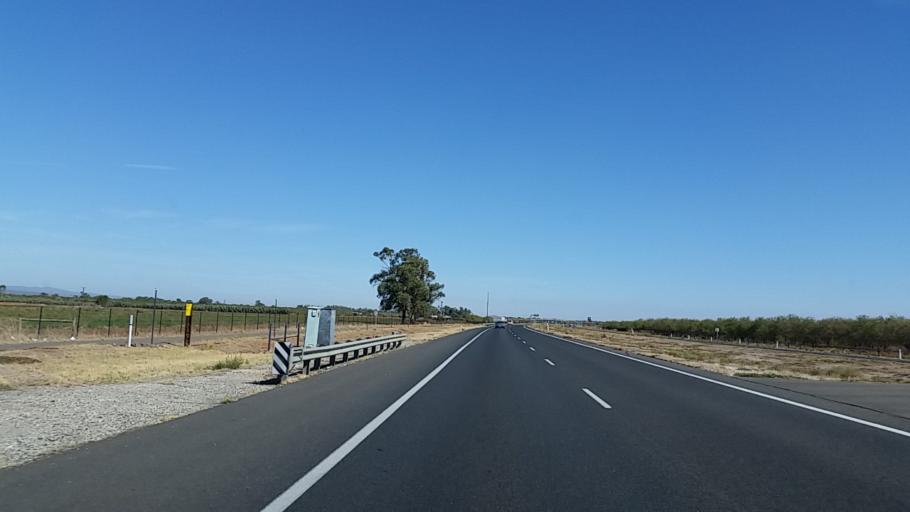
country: AU
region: South Australia
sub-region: Playford
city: Angle Vale
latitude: -34.6500
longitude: 138.6634
